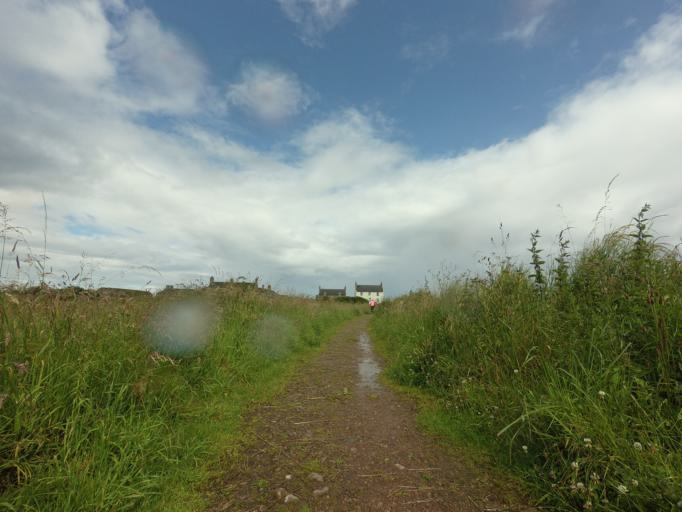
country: GB
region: Scotland
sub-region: Moray
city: Fochabers
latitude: 57.6720
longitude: -3.0923
